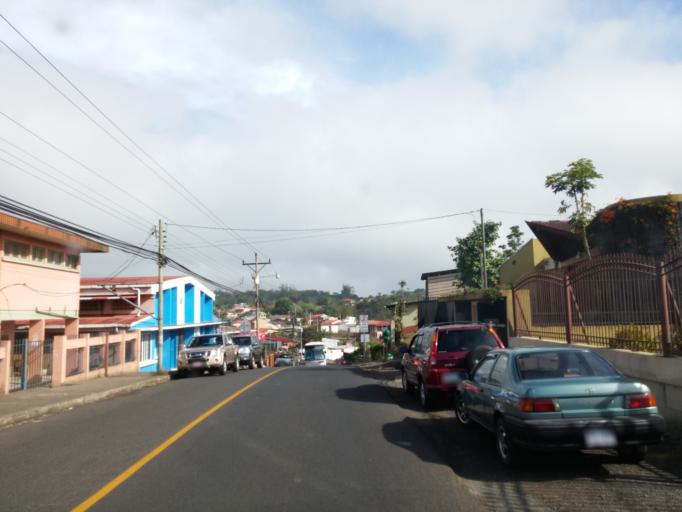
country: CR
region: Alajuela
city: San Ramon
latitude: 10.1071
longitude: -84.4658
